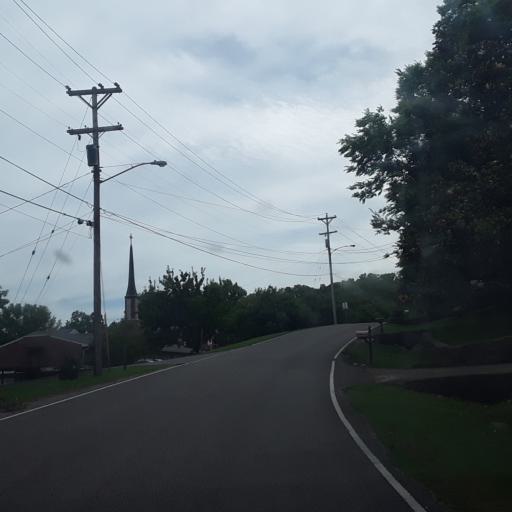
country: US
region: Tennessee
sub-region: Davidson County
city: Oak Hill
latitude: 36.0633
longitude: -86.7503
